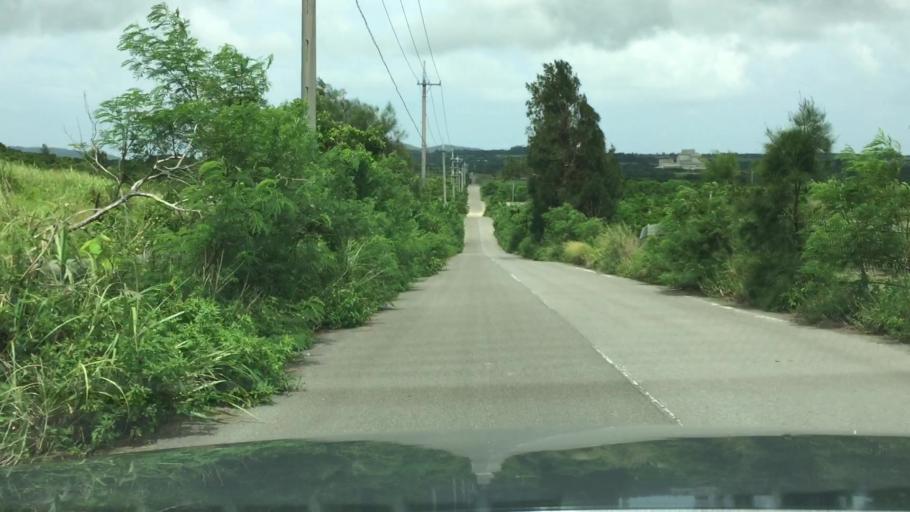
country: JP
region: Okinawa
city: Ishigaki
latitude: 24.3963
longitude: 124.1842
